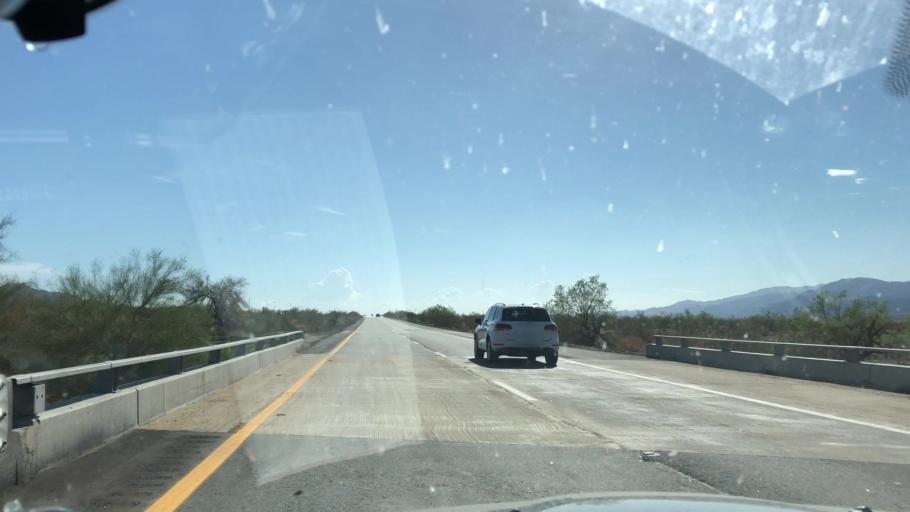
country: US
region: California
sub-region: Imperial County
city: Niland
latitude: 33.6906
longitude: -115.5065
